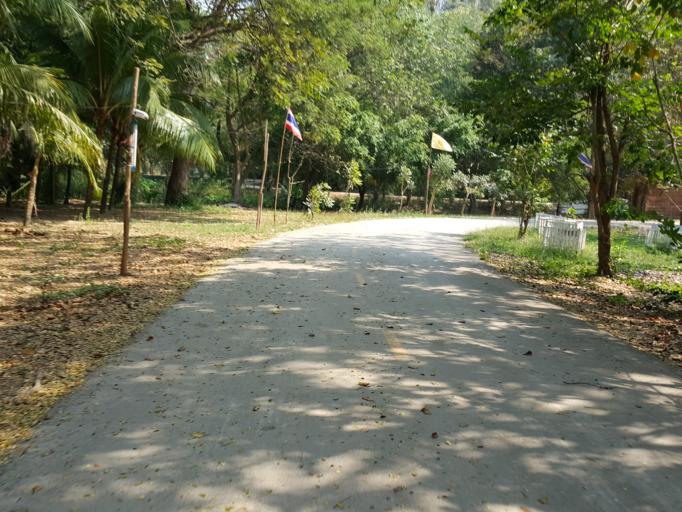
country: TH
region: Sukhothai
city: Thung Saliam
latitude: 17.3232
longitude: 99.5060
